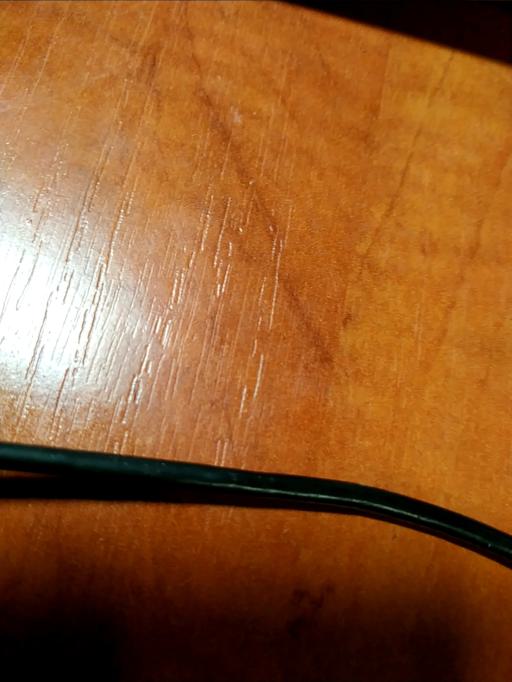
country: RU
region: Novgorod
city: Uglovka
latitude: 58.2850
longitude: 33.6065
